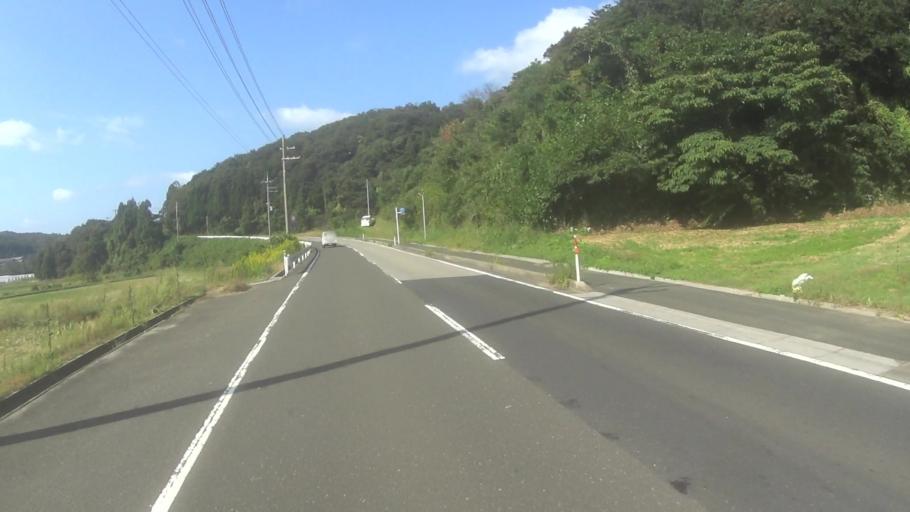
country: JP
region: Kyoto
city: Miyazu
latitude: 35.6911
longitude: 135.0512
